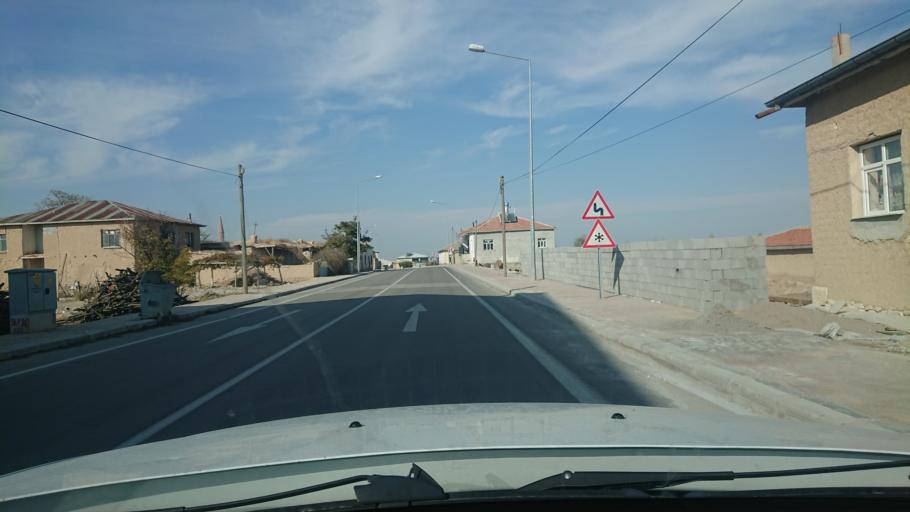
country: TR
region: Aksaray
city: Sultanhani
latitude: 38.2634
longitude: 33.4428
